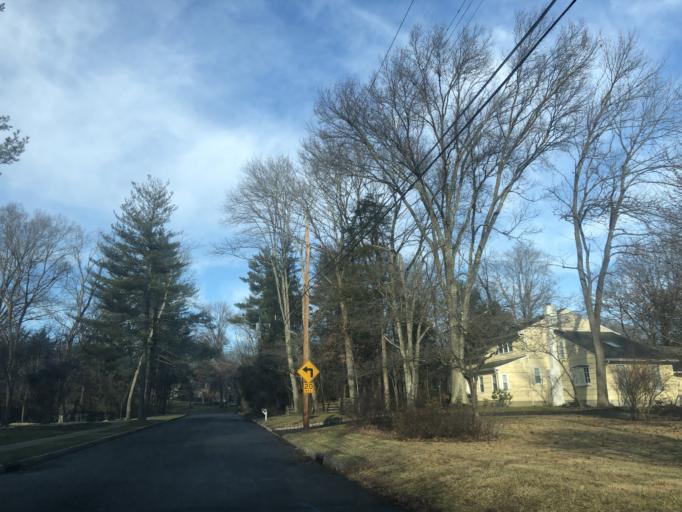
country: US
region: New Jersey
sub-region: Somerset County
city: Kingston
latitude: 40.3699
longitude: -74.6290
